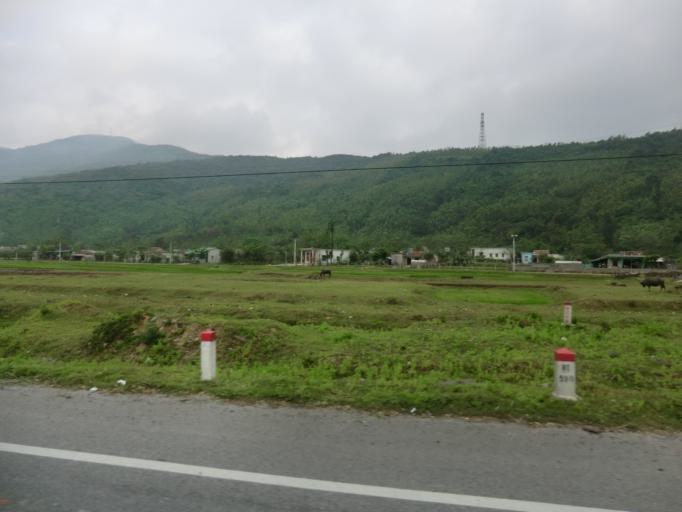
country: VN
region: Ha Tinh
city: Ky Anh
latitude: 17.9793
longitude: 106.4773
